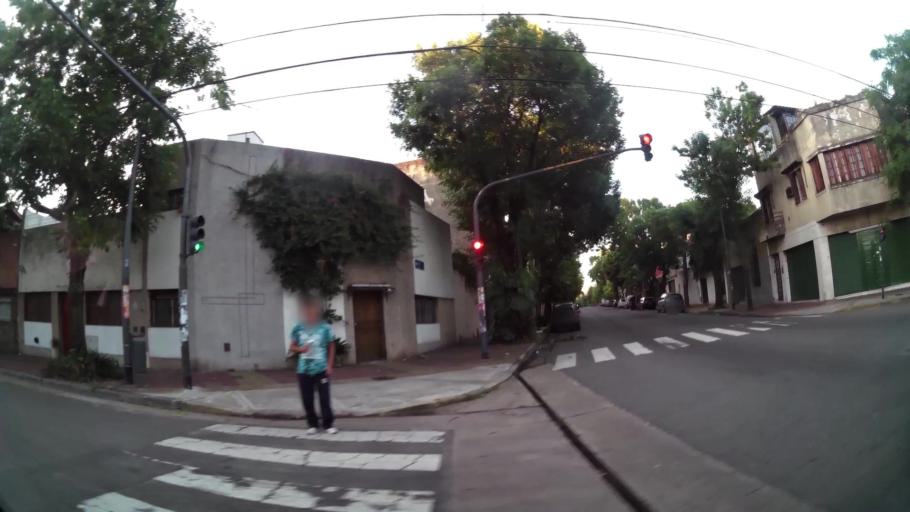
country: AR
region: Buenos Aires F.D.
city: Buenos Aires
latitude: -34.6337
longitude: -58.4146
